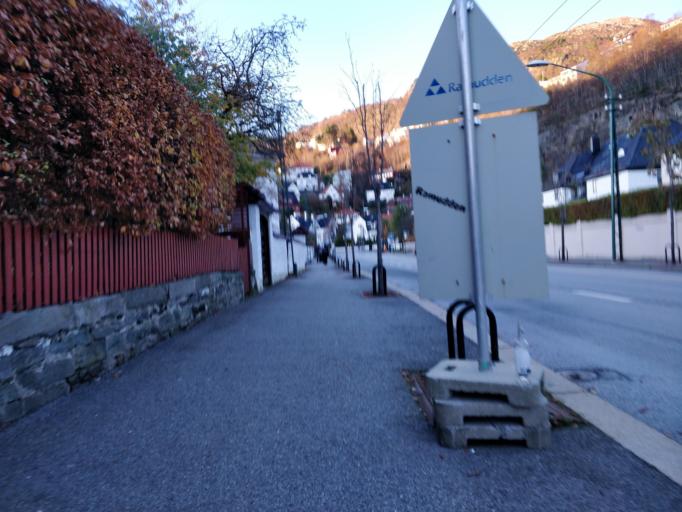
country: NO
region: Hordaland
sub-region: Bergen
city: Bergen
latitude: 60.3828
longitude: 5.3583
